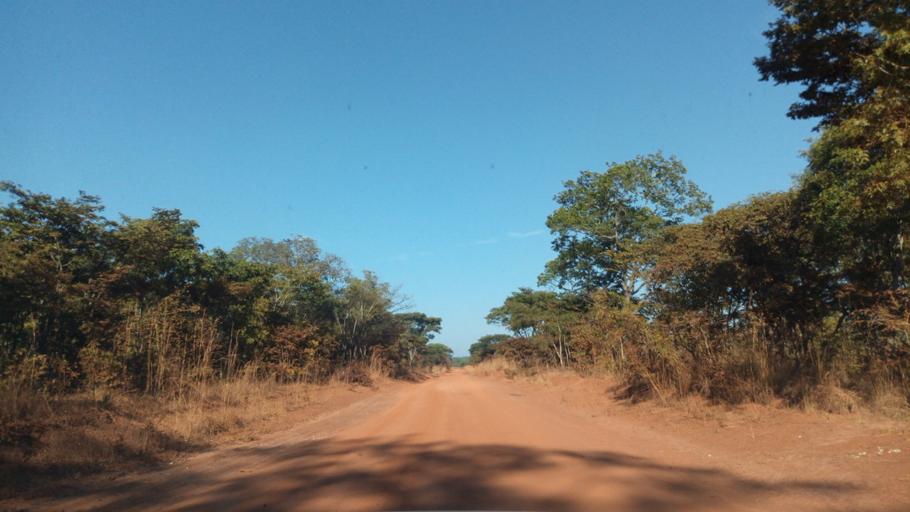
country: ZM
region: Luapula
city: Mwense
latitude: -10.6049
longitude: 28.4196
